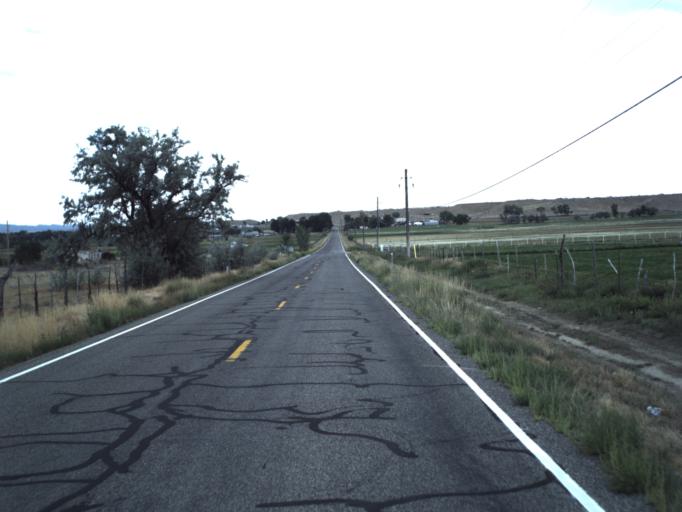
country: US
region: Utah
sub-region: Emery County
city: Huntington
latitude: 39.3838
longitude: -110.8524
